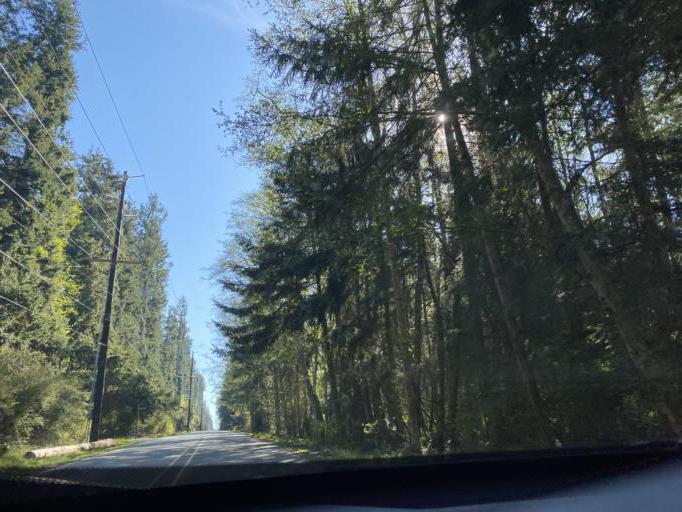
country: US
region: Washington
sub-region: Island County
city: Freeland
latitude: 48.0796
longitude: -122.6030
